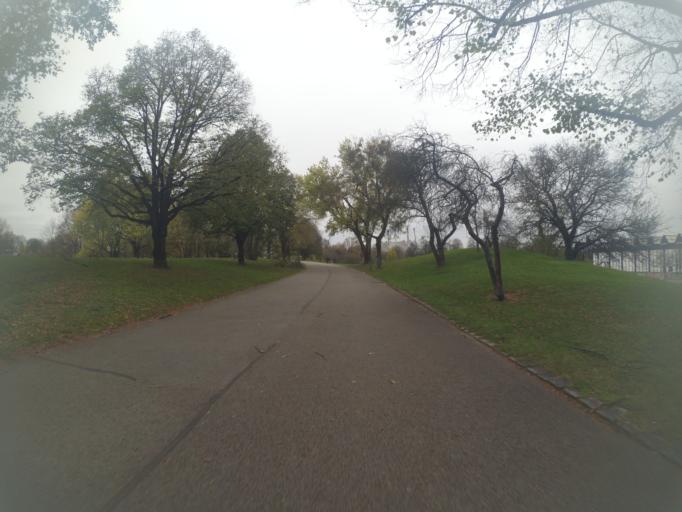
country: DE
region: Bavaria
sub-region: Upper Bavaria
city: Munich
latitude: 48.1793
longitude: 11.5474
